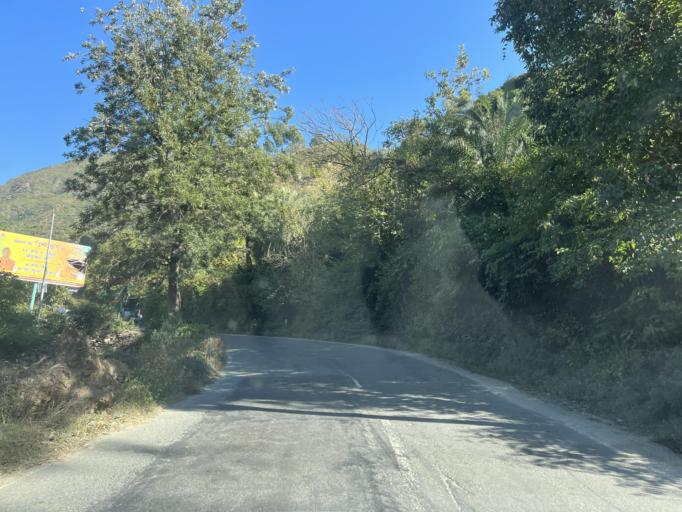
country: IN
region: Uttarakhand
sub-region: Almora
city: Ranikhet
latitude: 29.5227
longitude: 79.4821
